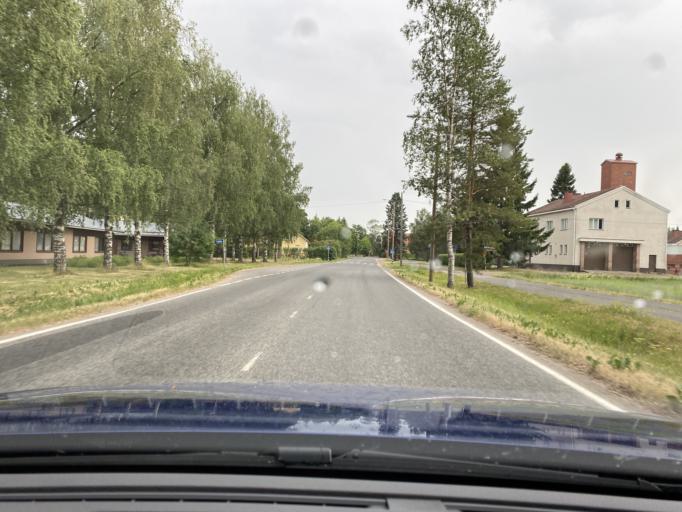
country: FI
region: Satakunta
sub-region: Rauma
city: Eura
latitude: 61.1358
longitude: 22.1275
